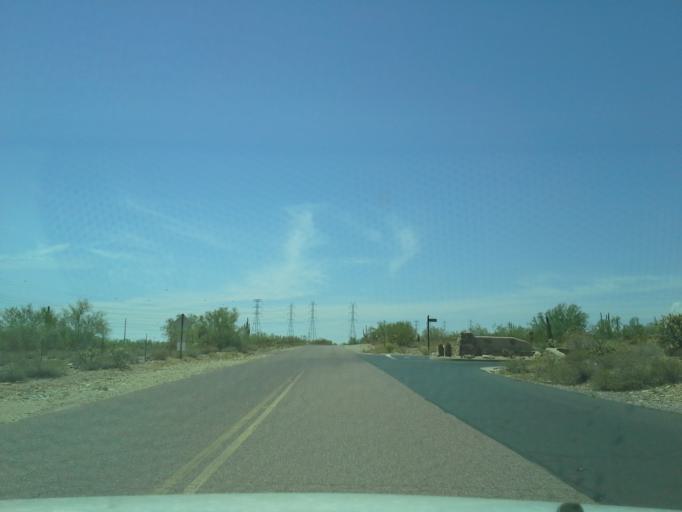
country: US
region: Arizona
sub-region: Maricopa County
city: Scottsdale
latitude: 33.5990
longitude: -111.8416
